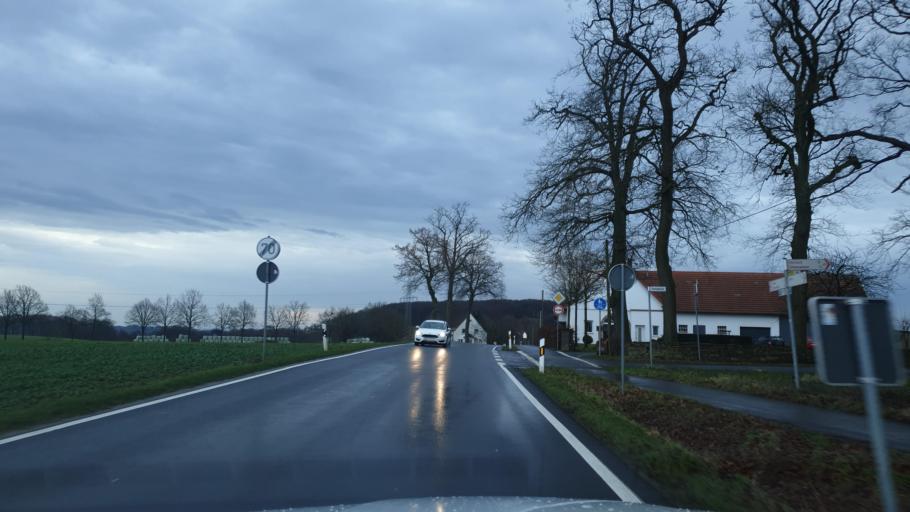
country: DE
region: North Rhine-Westphalia
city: Bad Oeynhausen
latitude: 52.1631
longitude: 8.8024
